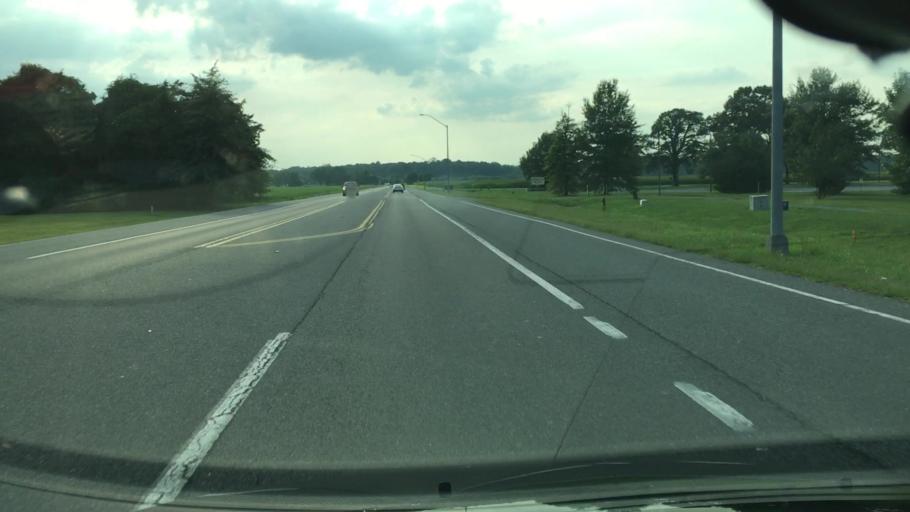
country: US
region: Maryland
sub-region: Worcester County
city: Ocean Pines
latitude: 38.3891
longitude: -75.1918
